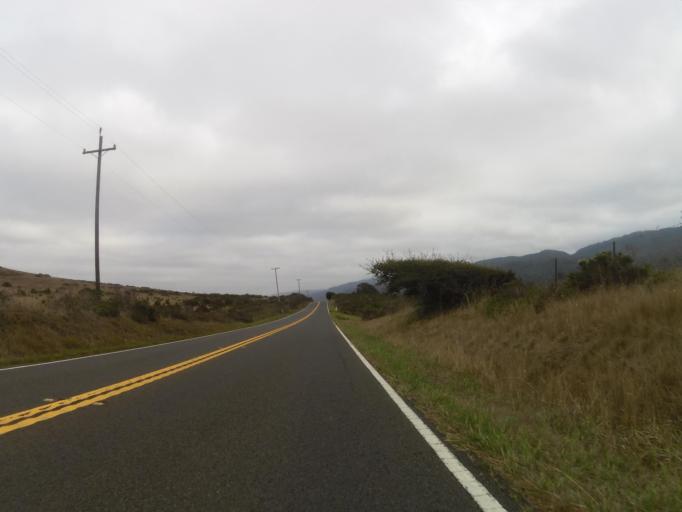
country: US
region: California
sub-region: Marin County
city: Inverness
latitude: 38.1210
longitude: -122.8557
